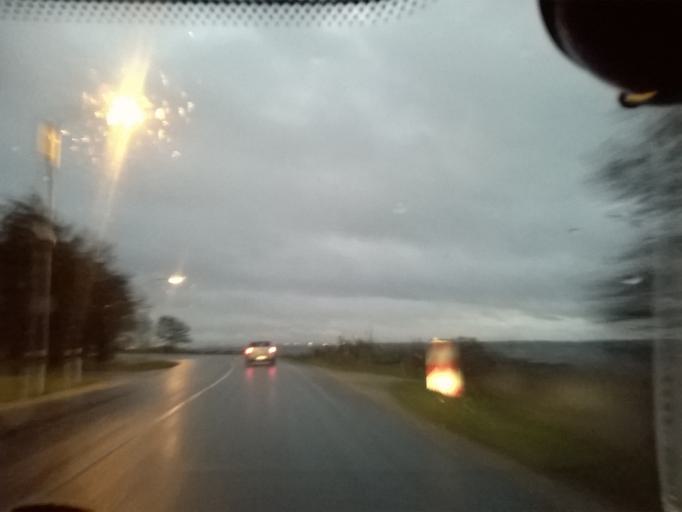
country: EE
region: Harju
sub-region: Viimsi vald
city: Rummu
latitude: 59.5365
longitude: 24.7933
